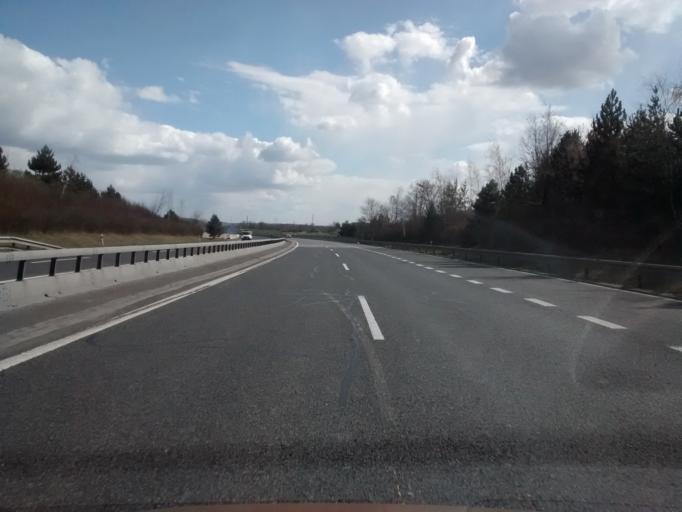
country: CZ
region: Central Bohemia
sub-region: Okres Melnik
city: Veltrusy
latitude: 50.3110
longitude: 14.3159
